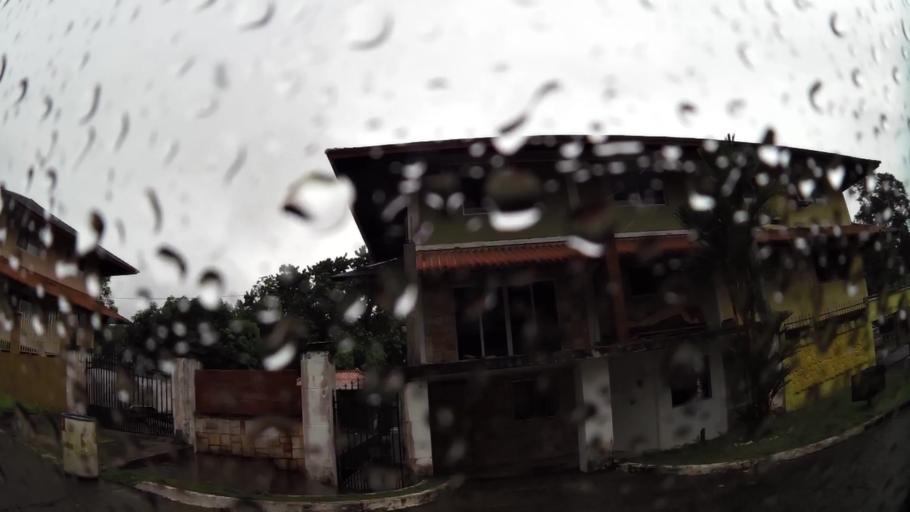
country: PA
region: Colon
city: Las Margaritas
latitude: 9.3135
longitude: -79.8705
